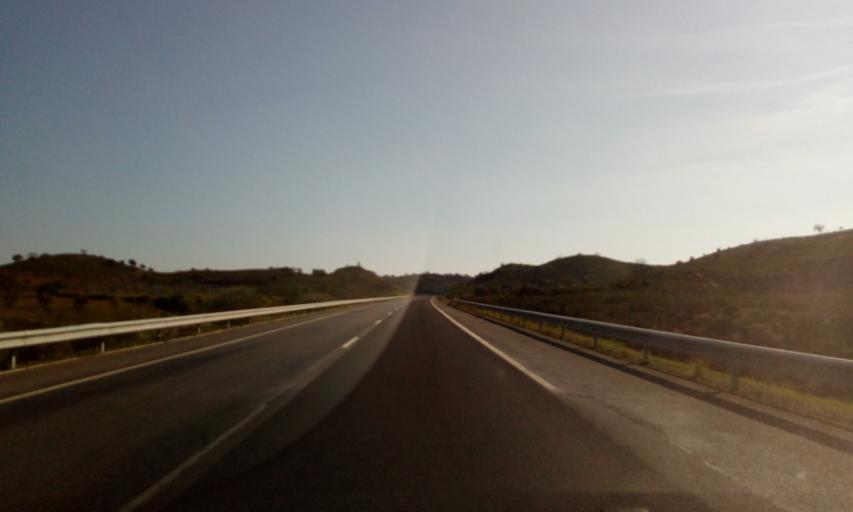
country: PT
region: Faro
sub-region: Castro Marim
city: Castro Marim
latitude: 37.2499
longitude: -7.4738
